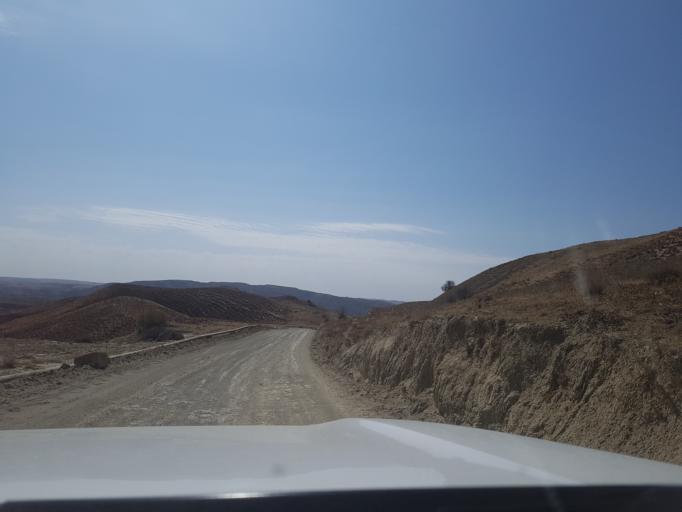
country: TM
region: Ahal
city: Baharly
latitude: 38.2491
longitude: 56.8924
